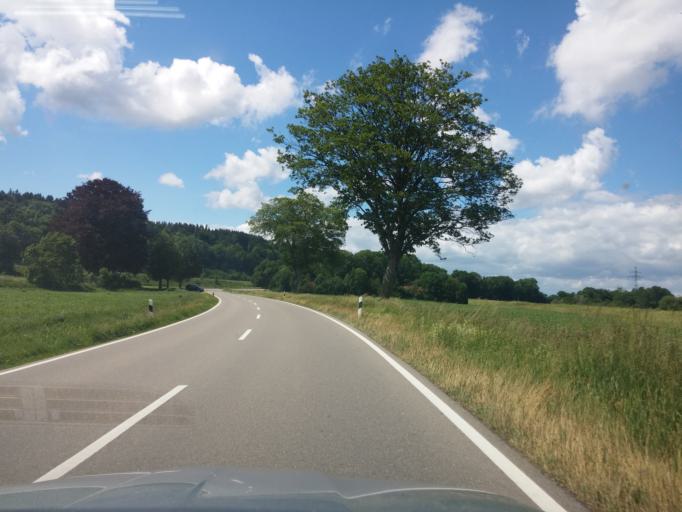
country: DE
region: Bavaria
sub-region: Swabia
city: Lautrach
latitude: 47.9081
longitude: 10.1186
